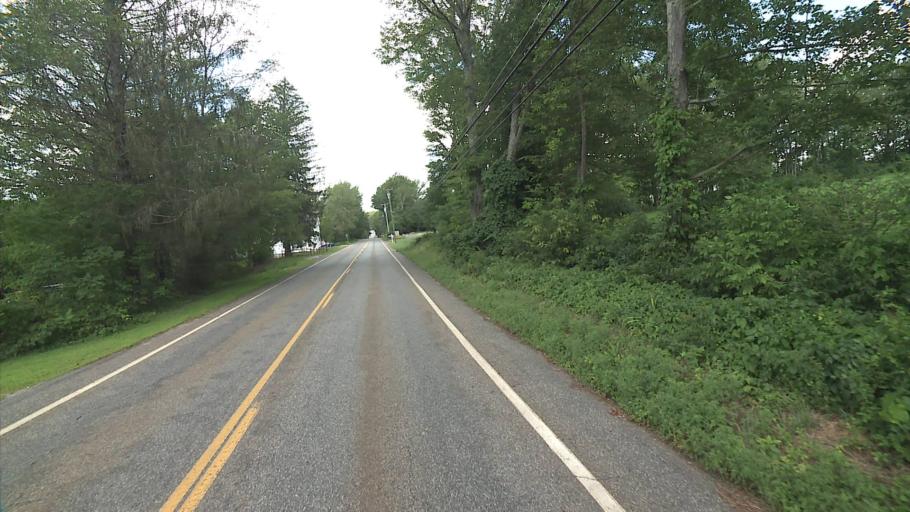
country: US
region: Connecticut
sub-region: Tolland County
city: Storrs
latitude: 41.9161
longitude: -72.1742
